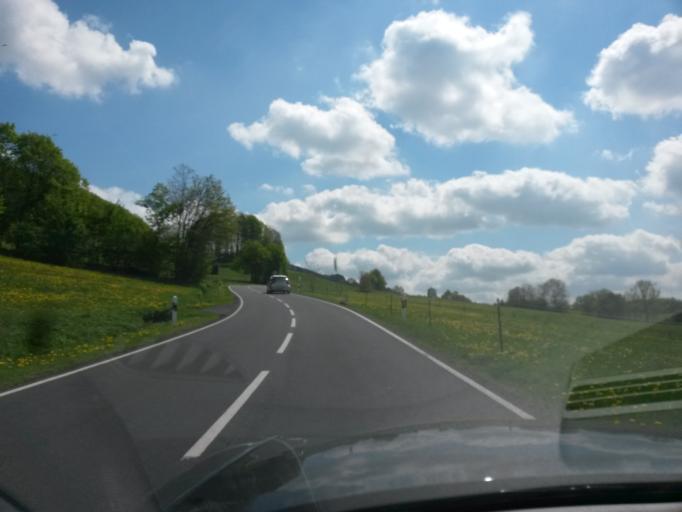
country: DE
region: Hesse
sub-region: Regierungsbezirk Kassel
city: Gersfeld
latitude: 50.5045
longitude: 9.9194
